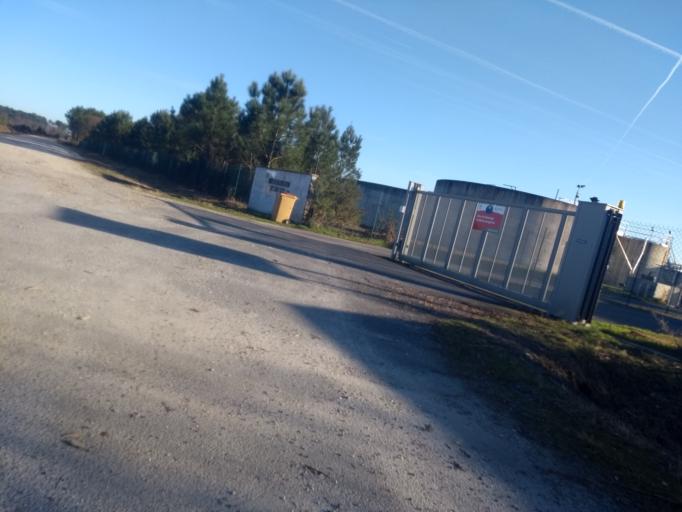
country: FR
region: Aquitaine
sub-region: Departement de la Gironde
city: Le Barp
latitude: 44.6164
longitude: -0.7936
